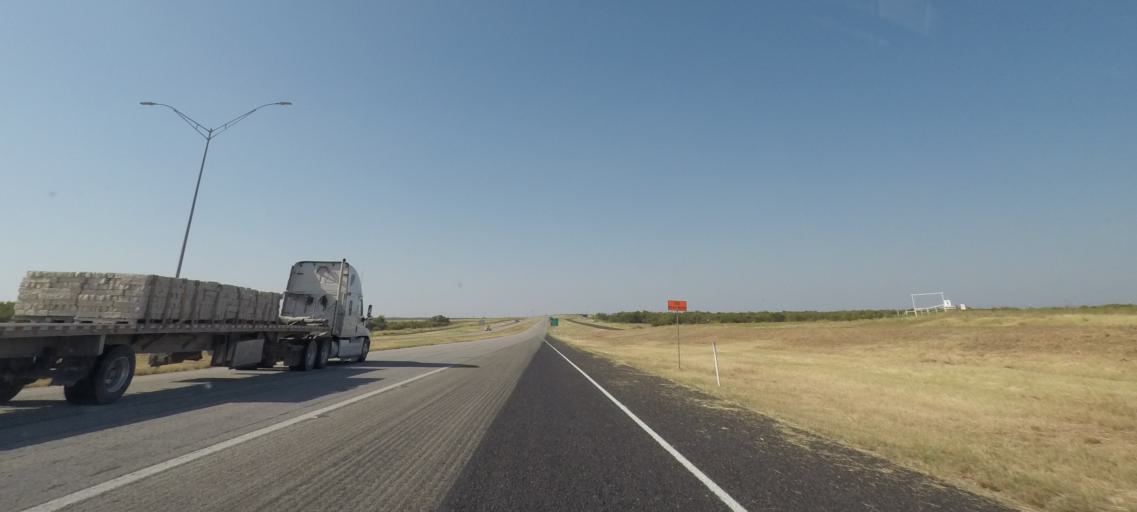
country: US
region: Texas
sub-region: Baylor County
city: Seymour
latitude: 33.6025
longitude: -99.2418
